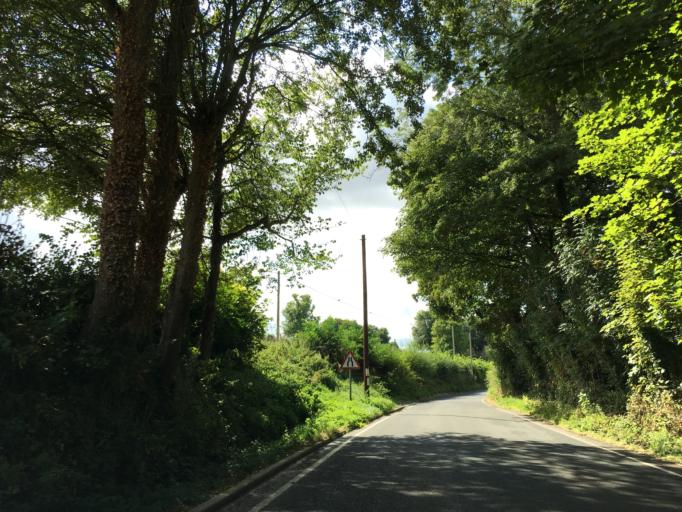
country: GB
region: England
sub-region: Hampshire
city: Kings Worthy
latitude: 51.1705
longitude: -1.3778
